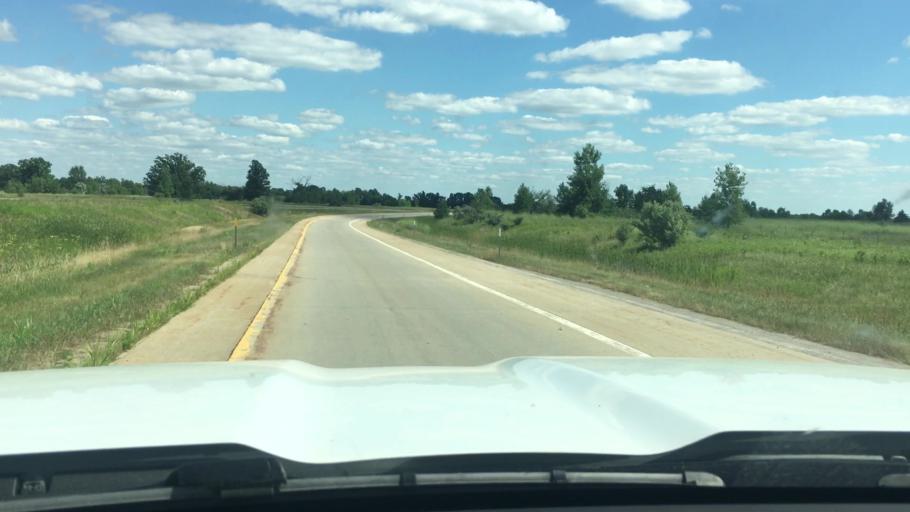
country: US
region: Michigan
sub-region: Gratiot County
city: Ithaca
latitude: 43.1739
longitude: -84.5659
